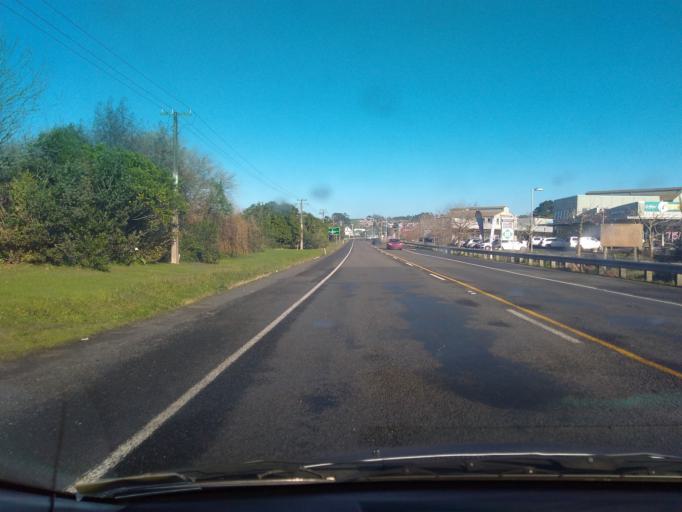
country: NZ
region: Auckland
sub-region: Auckland
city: Muriwai Beach
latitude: -36.7673
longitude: 174.4956
